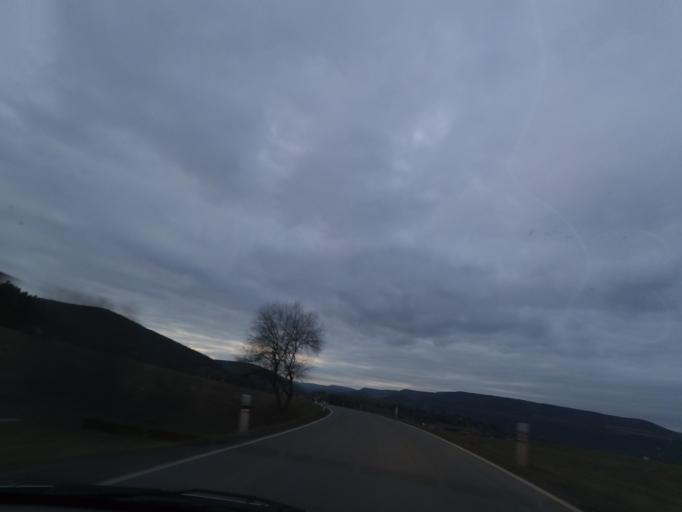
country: DE
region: Thuringia
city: Bad Blankenburg
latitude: 50.6649
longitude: 11.3034
